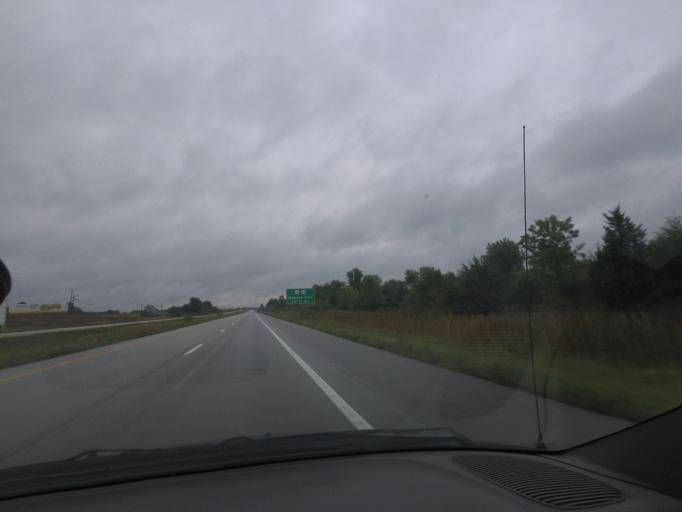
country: US
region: Missouri
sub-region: Marion County
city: Monroe City
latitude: 39.6645
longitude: -91.7319
